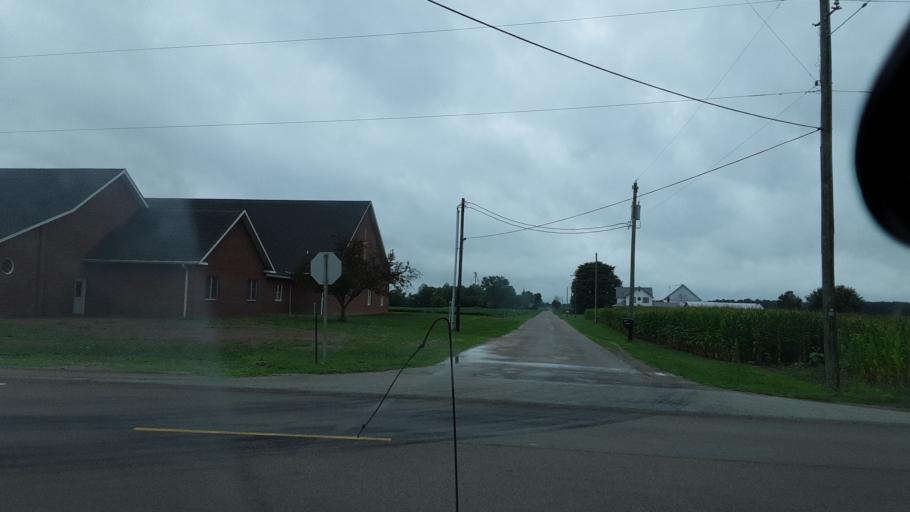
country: US
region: Ohio
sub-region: Van Wert County
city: Convoy
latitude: 40.8297
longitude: -84.7746
